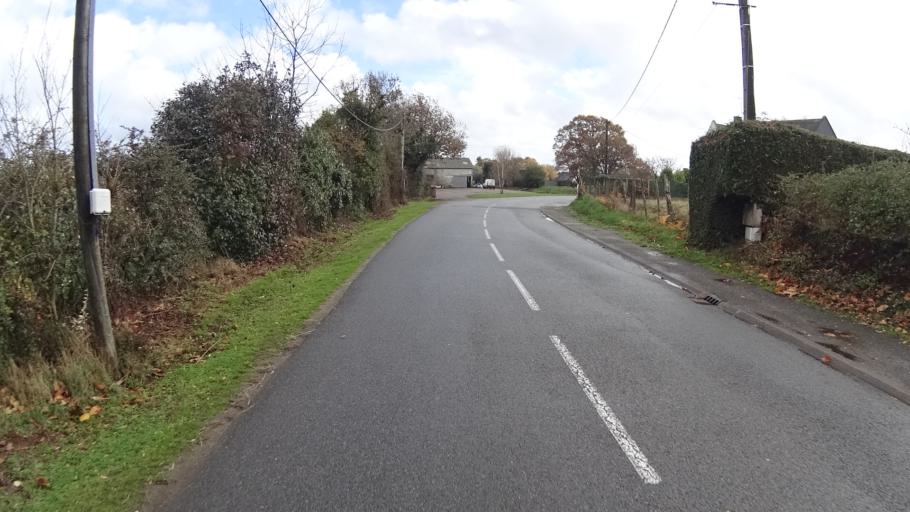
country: FR
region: Brittany
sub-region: Departement du Morbihan
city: Rieux
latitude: 47.5701
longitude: -2.1173
